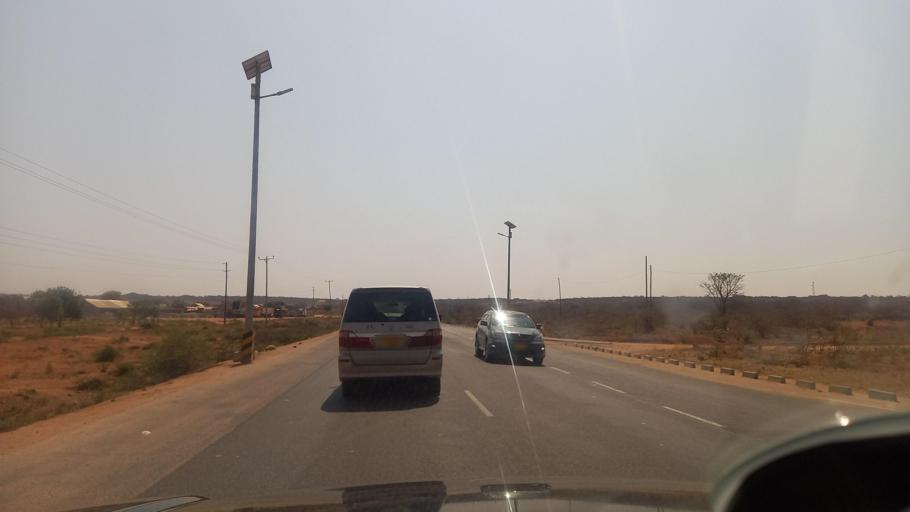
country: TZ
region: Dodoma
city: Kisasa
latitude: -6.1464
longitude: 35.8312
